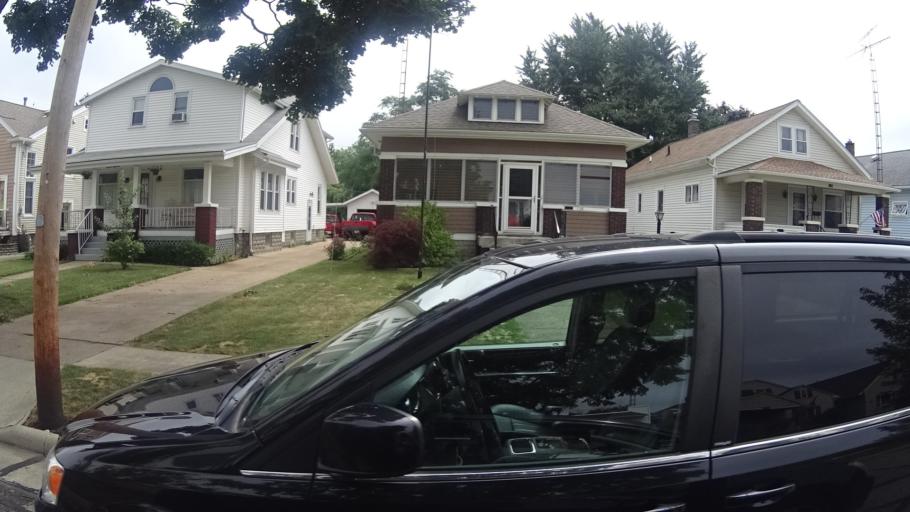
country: US
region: Ohio
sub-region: Erie County
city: Sandusky
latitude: 41.4478
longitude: -82.6916
